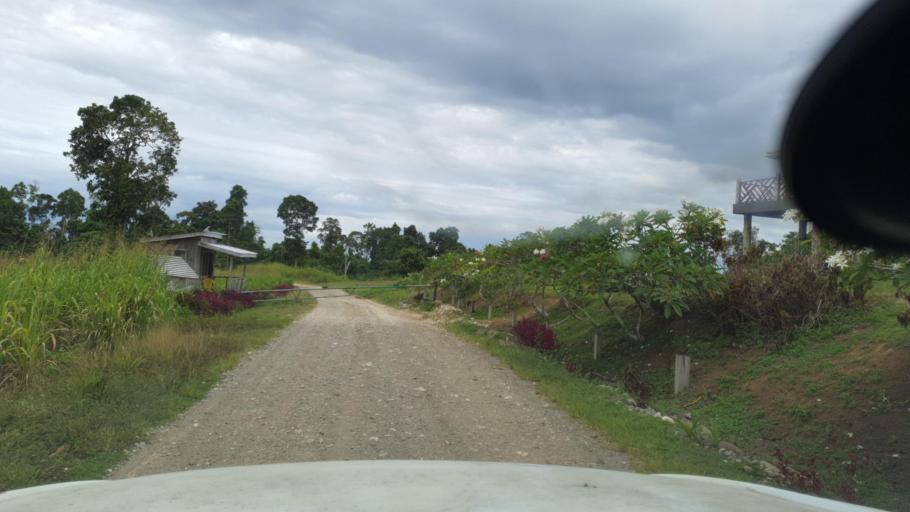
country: SB
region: Guadalcanal
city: Honiara
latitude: -9.4821
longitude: 160.0336
